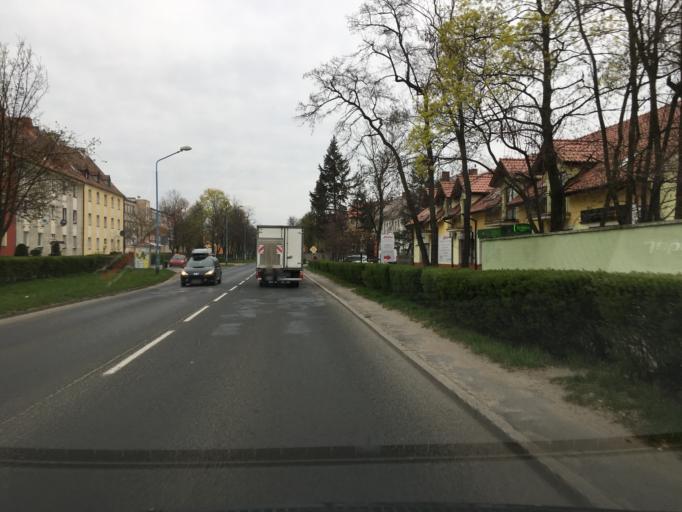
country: PL
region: Lower Silesian Voivodeship
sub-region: Legnica
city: Legnica
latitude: 51.1914
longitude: 16.1768
